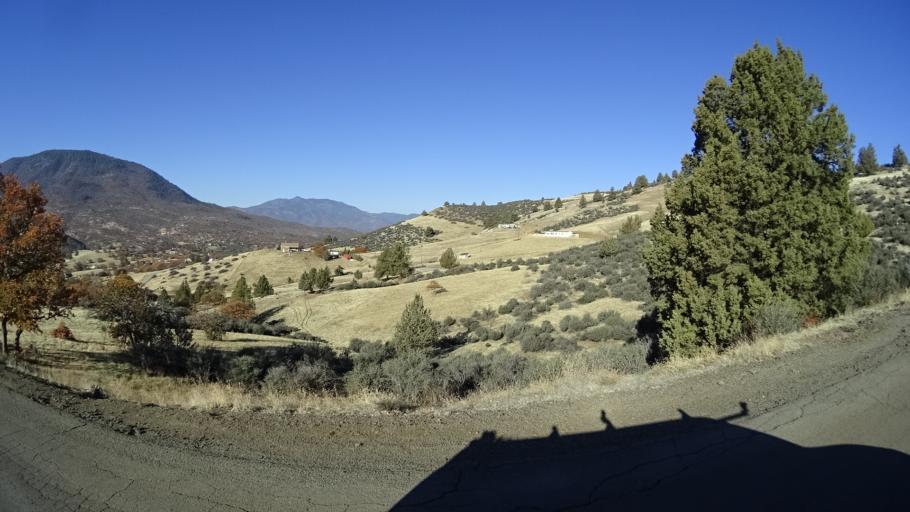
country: US
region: California
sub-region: Siskiyou County
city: Montague
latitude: 41.8787
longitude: -122.4591
